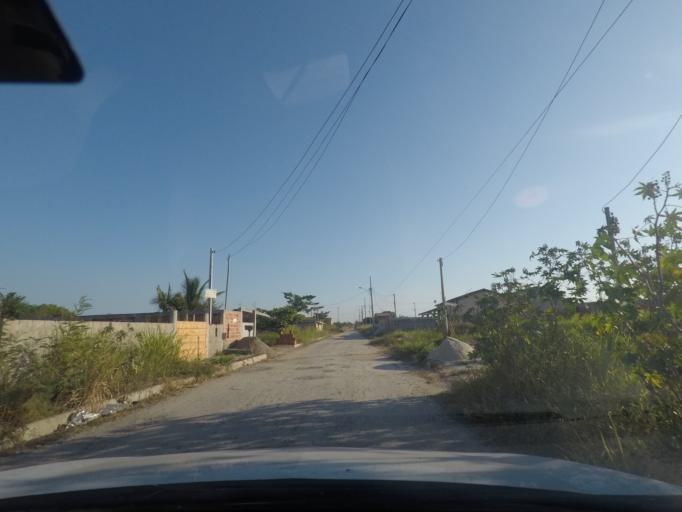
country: BR
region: Rio de Janeiro
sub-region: Marica
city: Marica
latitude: -22.9608
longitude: -42.9343
